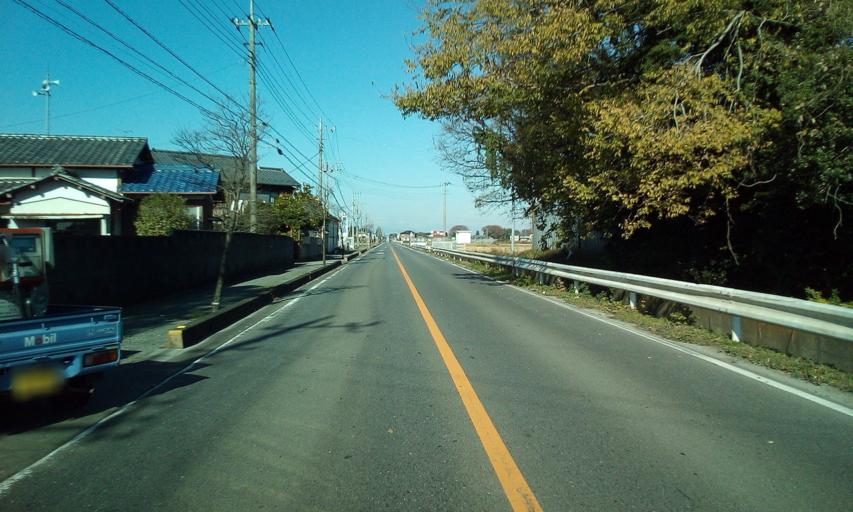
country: JP
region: Saitama
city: Kasukabe
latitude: 36.0229
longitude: 139.7897
